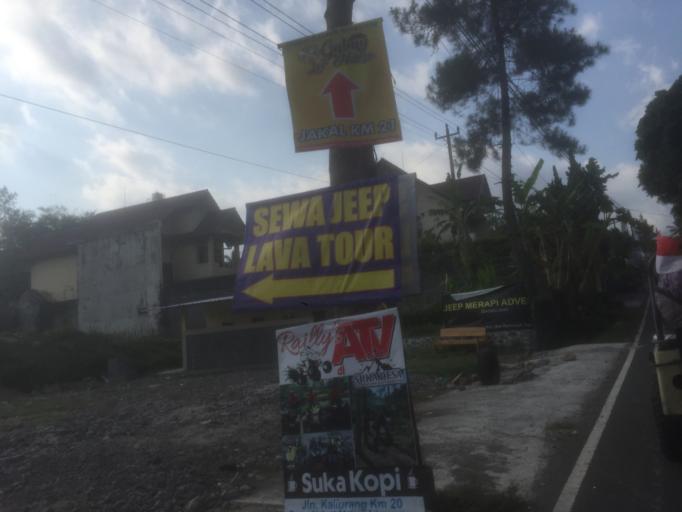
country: ID
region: Daerah Istimewa Yogyakarta
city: Sleman
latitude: -7.6451
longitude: 110.4244
